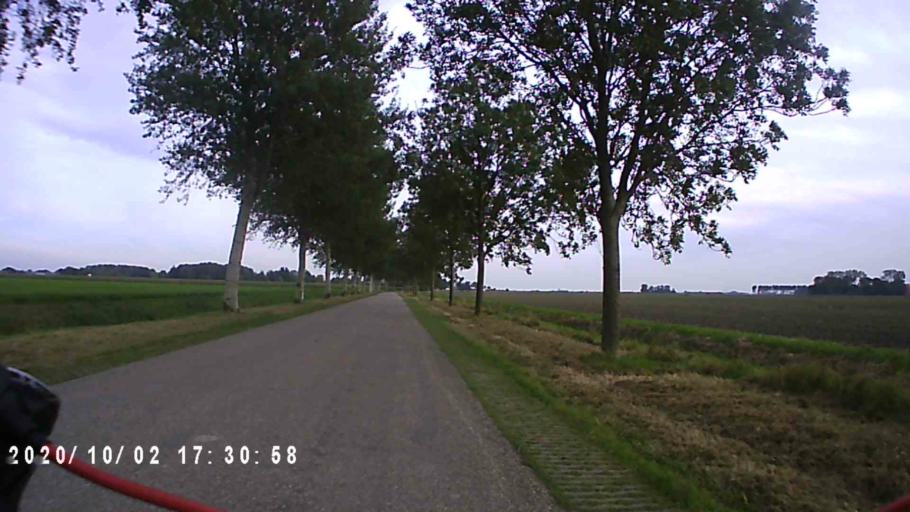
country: NL
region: Groningen
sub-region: Gemeente De Marne
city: Ulrum
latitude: 53.3367
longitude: 6.3299
